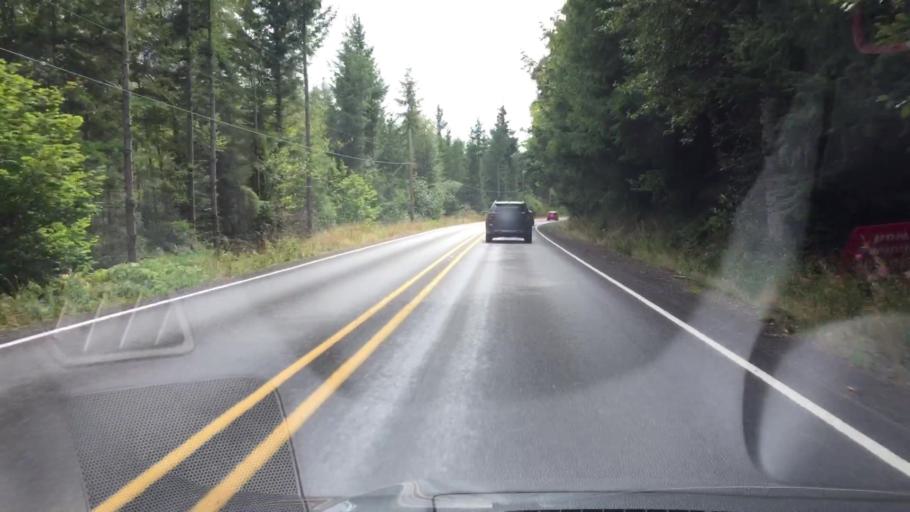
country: US
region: Washington
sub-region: Pierce County
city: Eatonville
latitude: 46.8332
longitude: -122.2514
